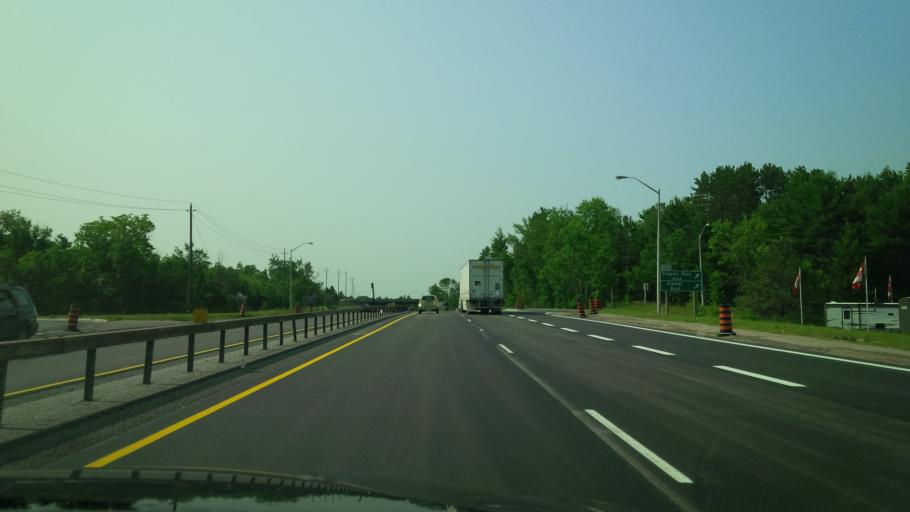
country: CA
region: Ontario
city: Gravenhurst
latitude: 44.7720
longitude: -79.3348
